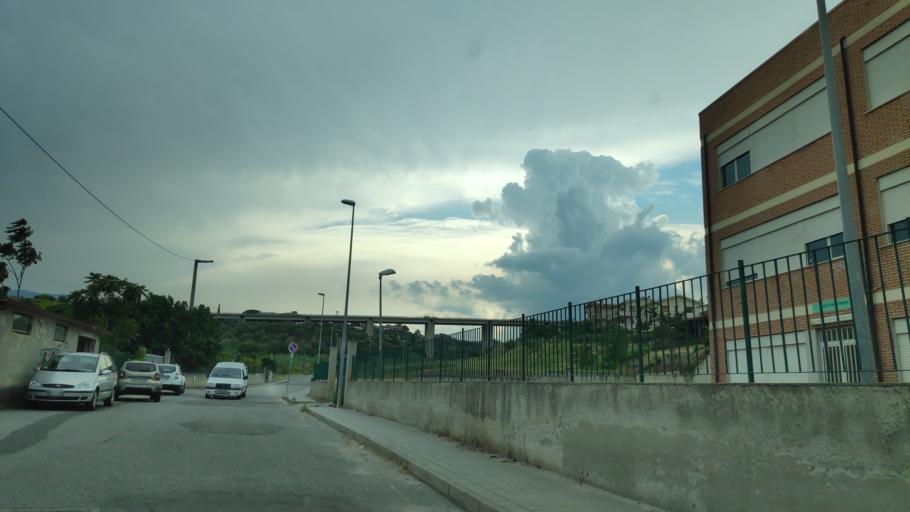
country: IT
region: Calabria
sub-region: Provincia di Catanzaro
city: Soverato Marina
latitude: 38.6838
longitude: 16.5477
